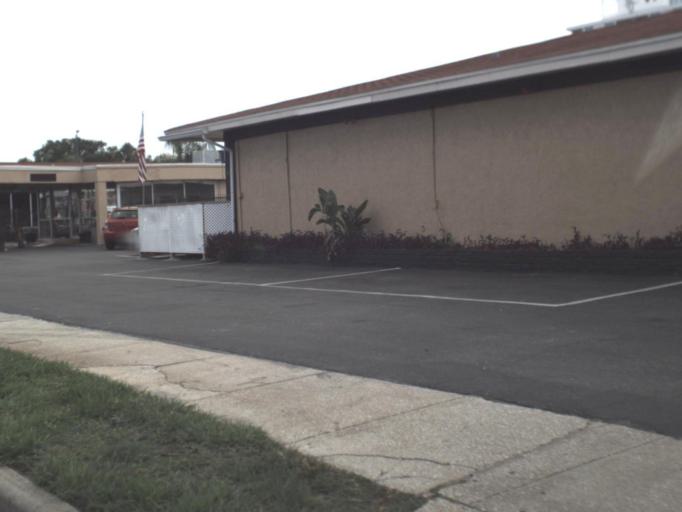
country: US
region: Florida
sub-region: Pinellas County
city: Saint Petersburg
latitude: 27.7757
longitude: -82.6793
